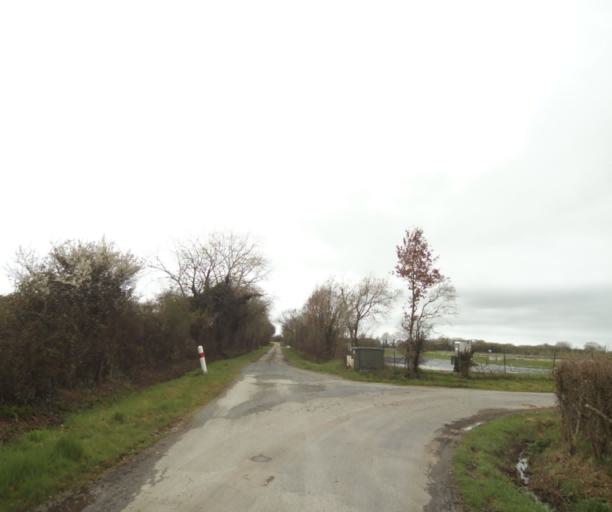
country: FR
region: Pays de la Loire
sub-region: Departement de la Loire-Atlantique
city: Bouvron
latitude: 47.4270
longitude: -1.8459
